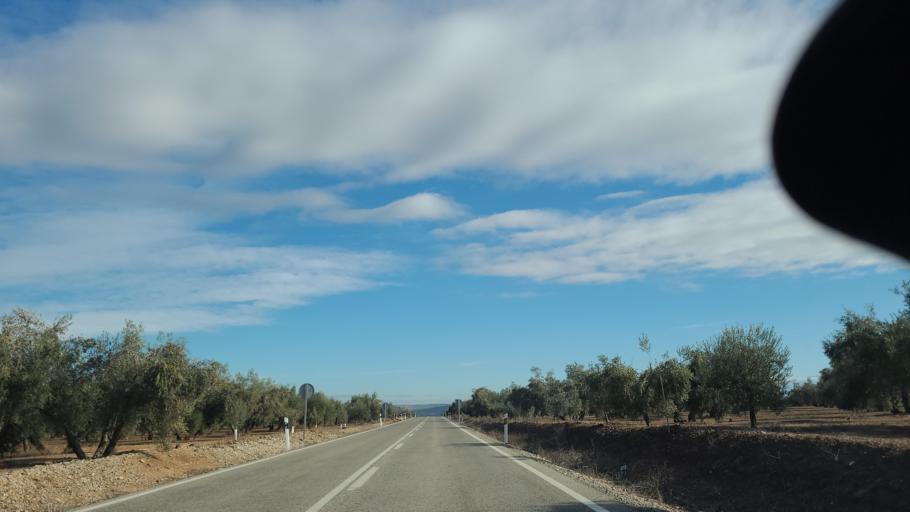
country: ES
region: Andalusia
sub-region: Provincia de Jaen
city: Espeluy
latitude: 38.0244
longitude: -3.8595
